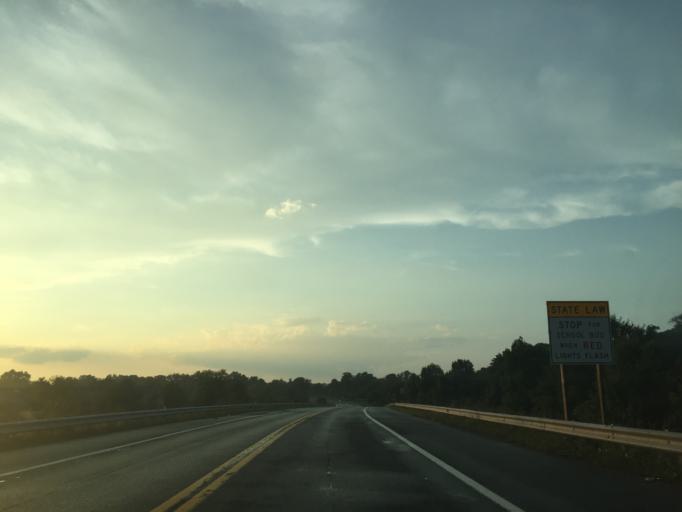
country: US
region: Maryland
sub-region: Harford County
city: Riverside
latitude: 39.4717
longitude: -76.2349
